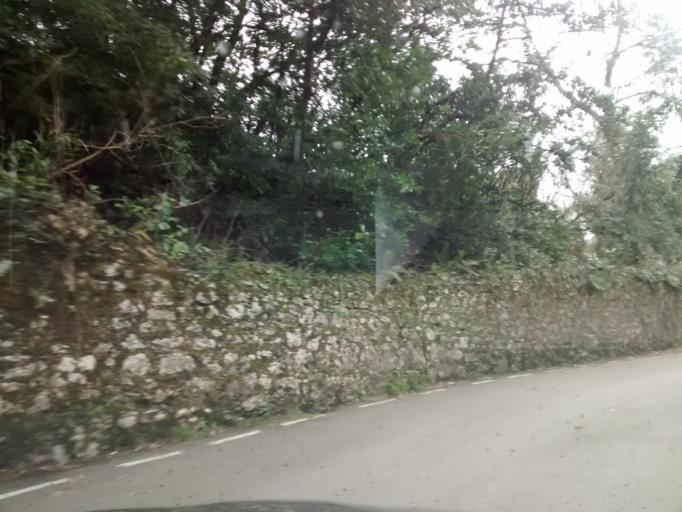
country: ES
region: Cantabria
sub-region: Provincia de Cantabria
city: Entrambasaguas
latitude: 43.3502
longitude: -3.7051
